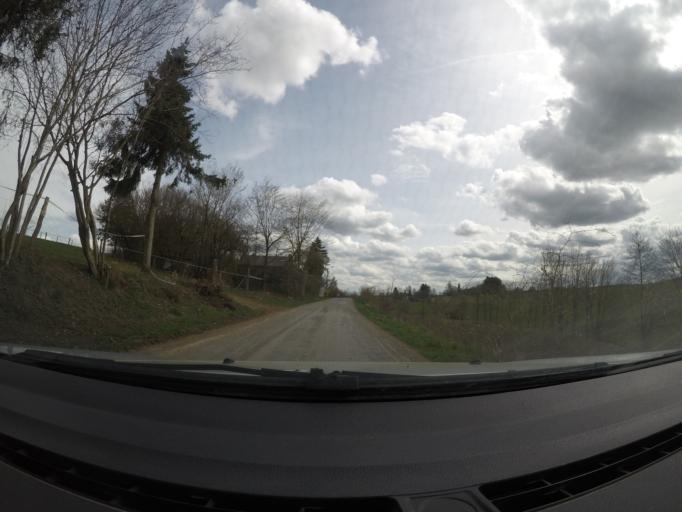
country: BE
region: Wallonia
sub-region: Province du Luxembourg
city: Neufchateau
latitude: 49.8150
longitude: 5.4762
